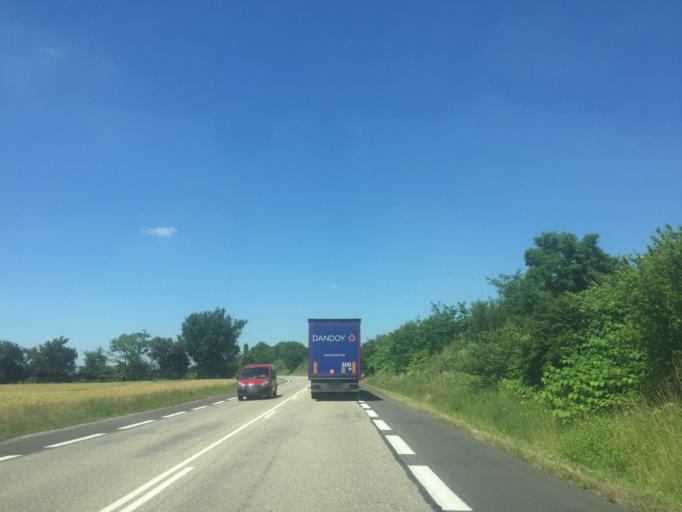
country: FR
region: Rhone-Alpes
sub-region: Departement du Rhone
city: Pusignan
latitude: 45.7420
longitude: 5.0759
